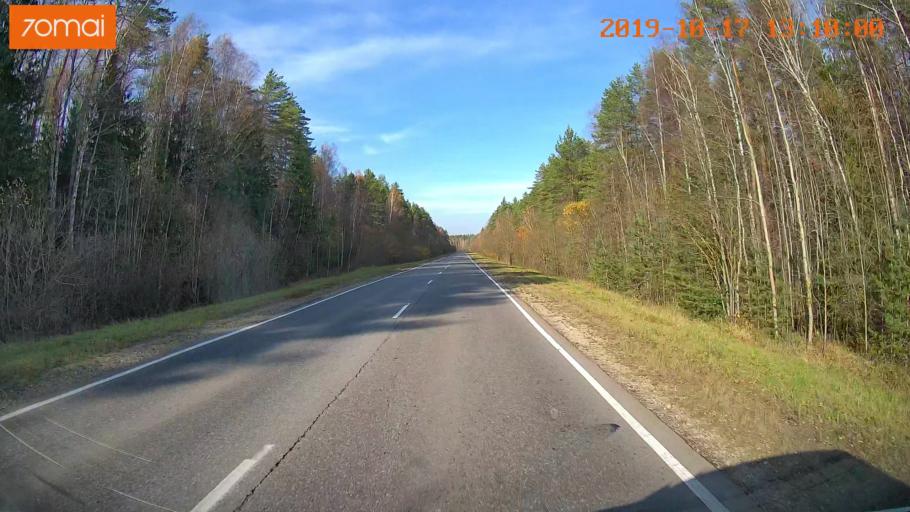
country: RU
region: Rjazan
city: Syntul
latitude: 55.0123
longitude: 41.2594
